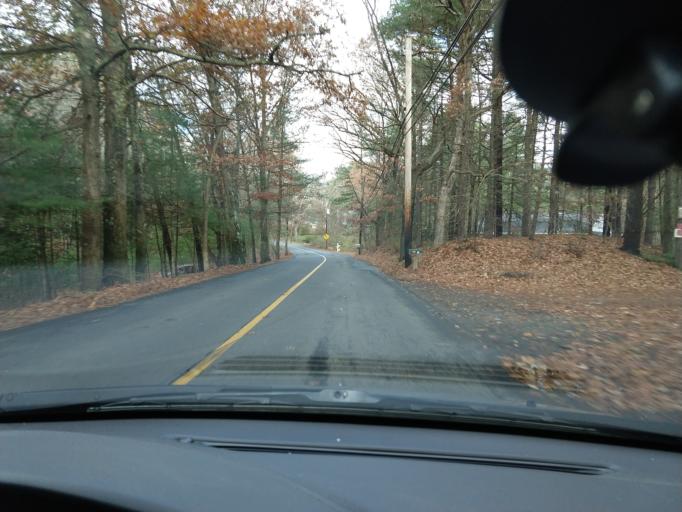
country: US
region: Massachusetts
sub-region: Middlesex County
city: West Concord
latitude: 42.4810
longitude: -71.3821
